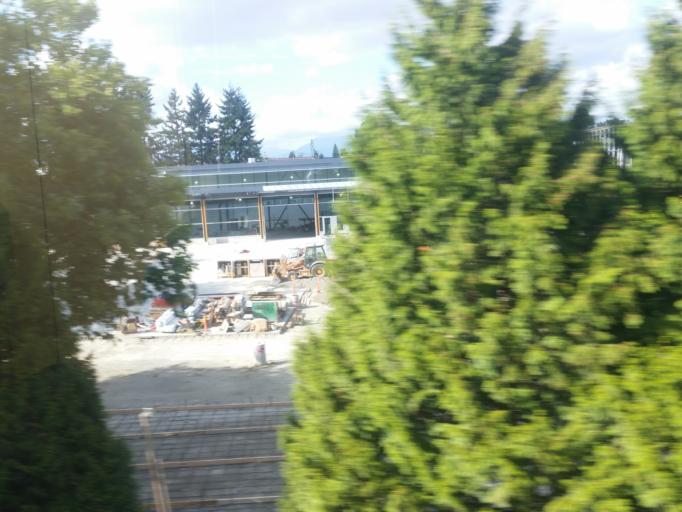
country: CA
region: British Columbia
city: Burnaby
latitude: 49.2150
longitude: -122.9714
